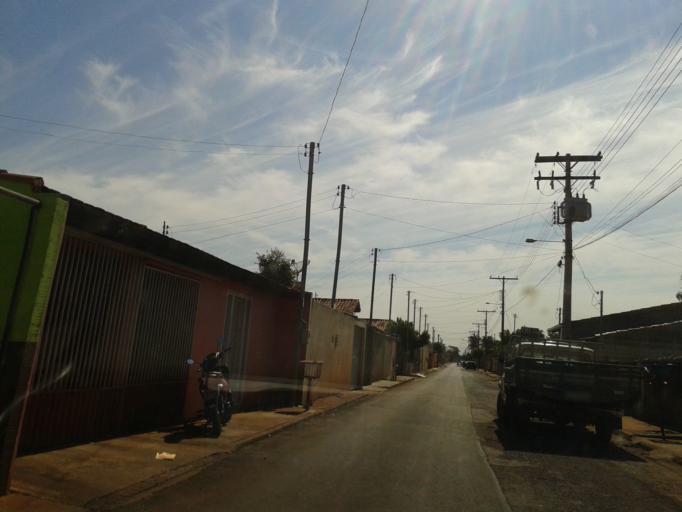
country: BR
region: Minas Gerais
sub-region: Santa Vitoria
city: Santa Vitoria
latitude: -19.0016
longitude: -50.5502
